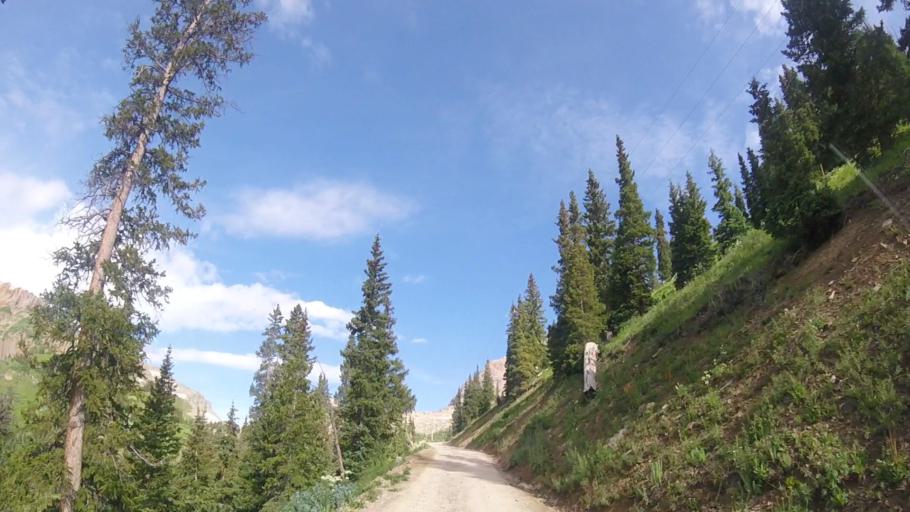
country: US
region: Colorado
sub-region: San Miguel County
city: Telluride
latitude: 37.8492
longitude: -107.7689
